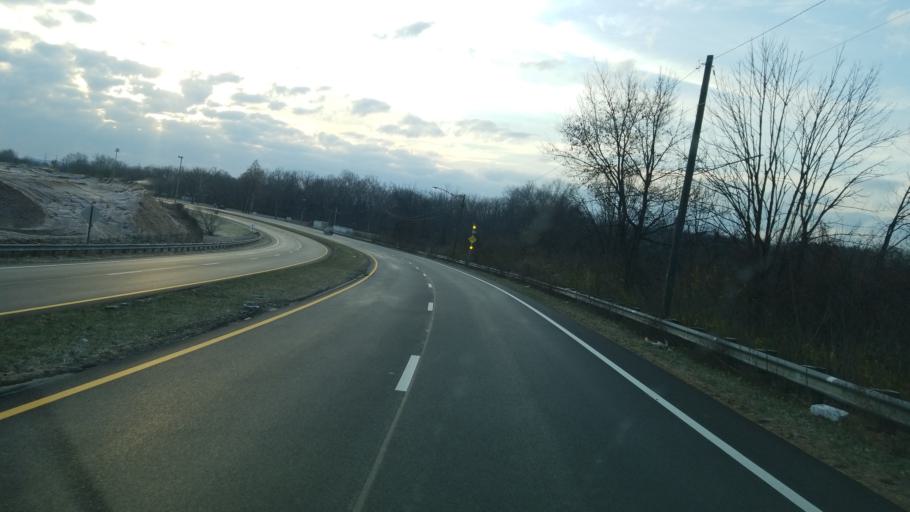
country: US
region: Ohio
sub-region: Ross County
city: Chillicothe
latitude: 39.3231
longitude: -82.9710
